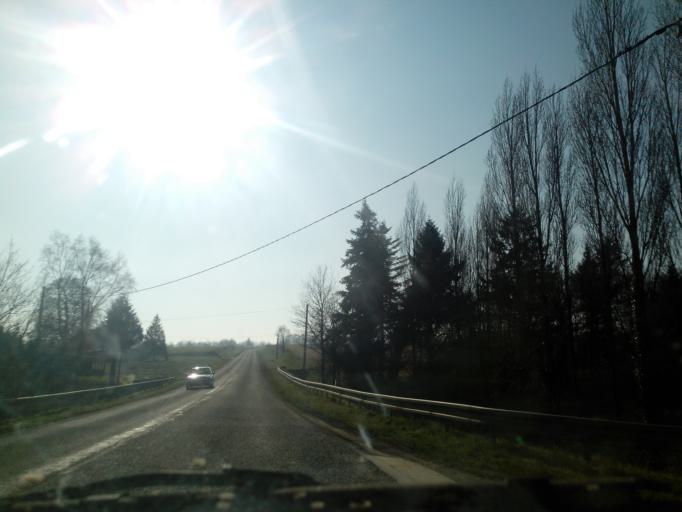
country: FR
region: Brittany
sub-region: Departement du Morbihan
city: Meneac
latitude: 48.1494
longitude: -2.4473
